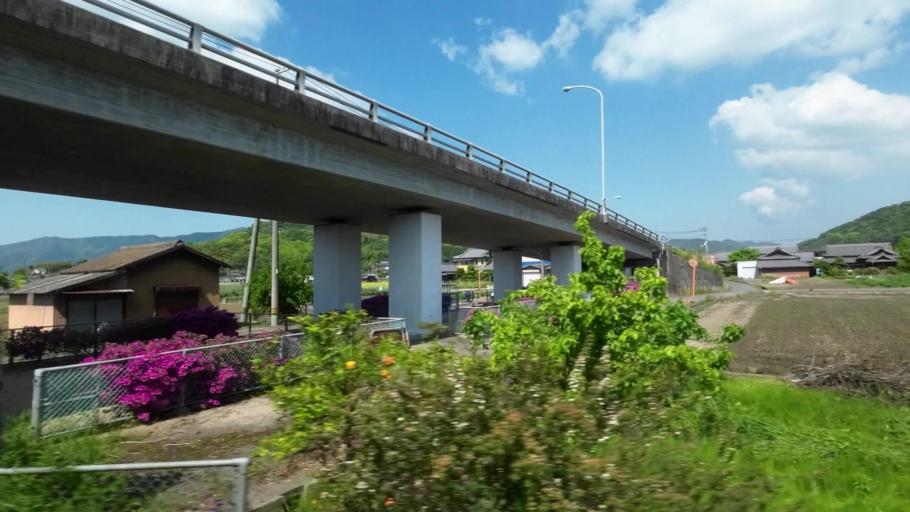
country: JP
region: Kagawa
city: Kan'onjicho
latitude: 34.1883
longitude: 133.7131
